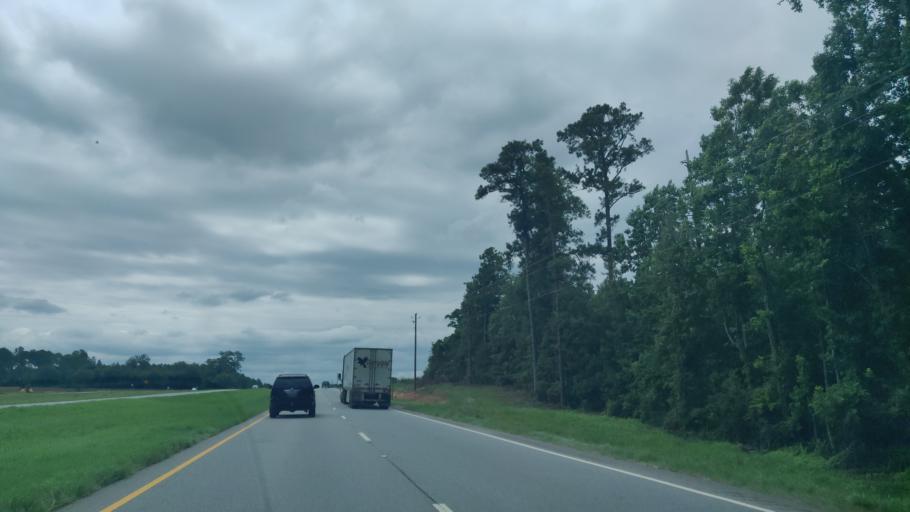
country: US
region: Georgia
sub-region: Terrell County
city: Dawson
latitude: 31.8388
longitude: -84.4687
